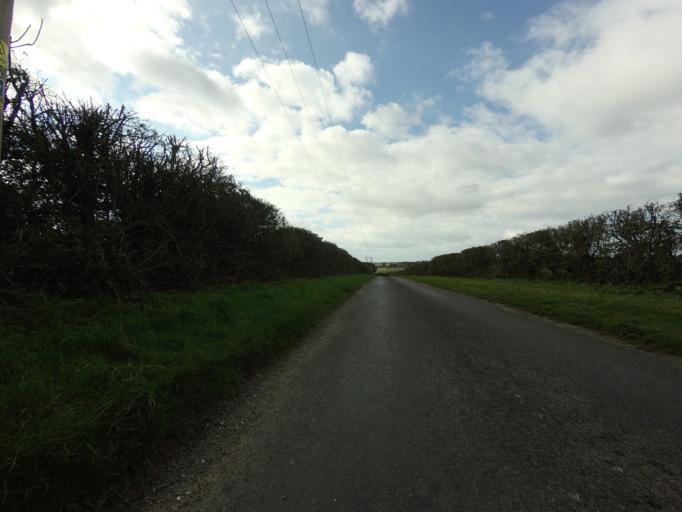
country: GB
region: England
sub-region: Norfolk
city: Hunstanton
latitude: 52.9357
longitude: 0.5834
